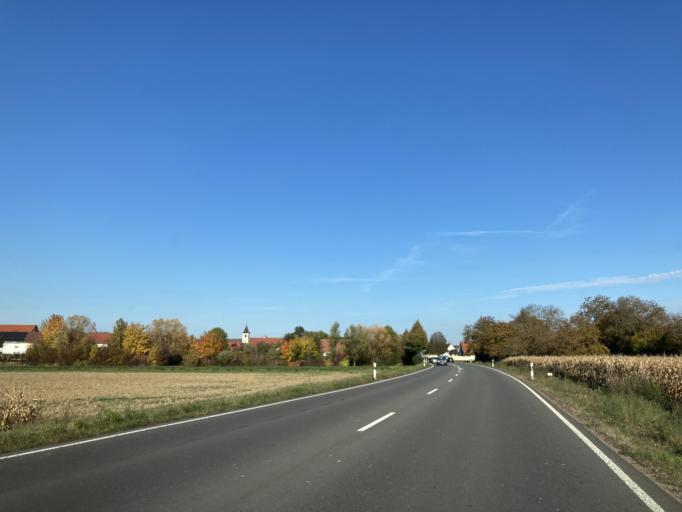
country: DE
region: Baden-Wuerttemberg
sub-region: Freiburg Region
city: Buggingen
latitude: 47.8559
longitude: 7.6362
